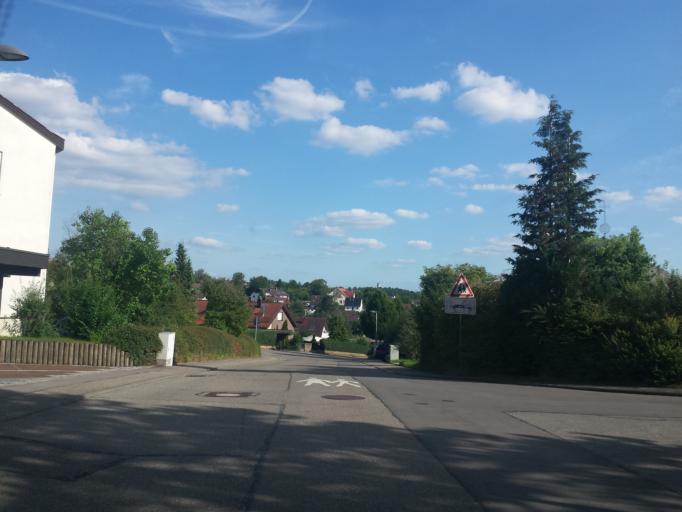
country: DE
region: Baden-Wuerttemberg
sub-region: Regierungsbezirk Stuttgart
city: Aidlingen
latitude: 48.7178
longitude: 8.9086
